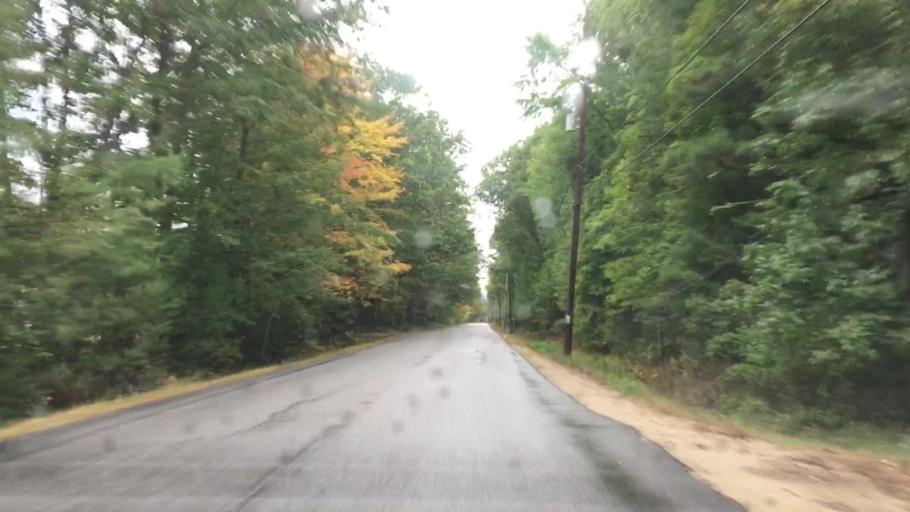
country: US
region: Maine
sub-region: Cumberland County
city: Harrison
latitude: 44.0685
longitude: -70.6321
